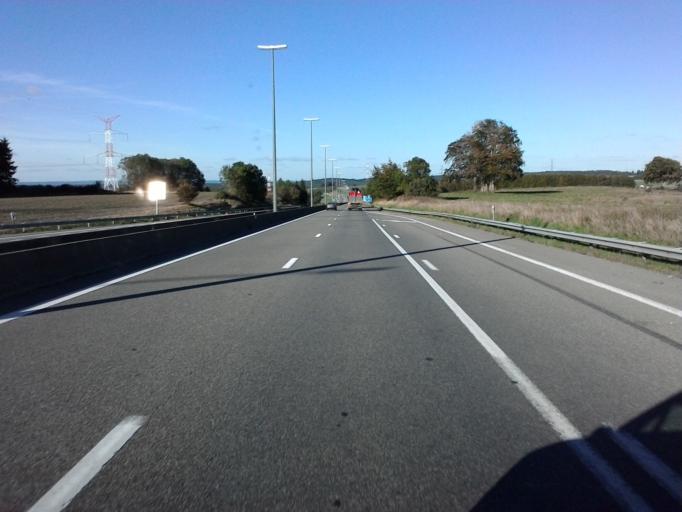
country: BE
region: Wallonia
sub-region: Province du Luxembourg
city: Bastogne
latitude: 50.0084
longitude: 5.6878
